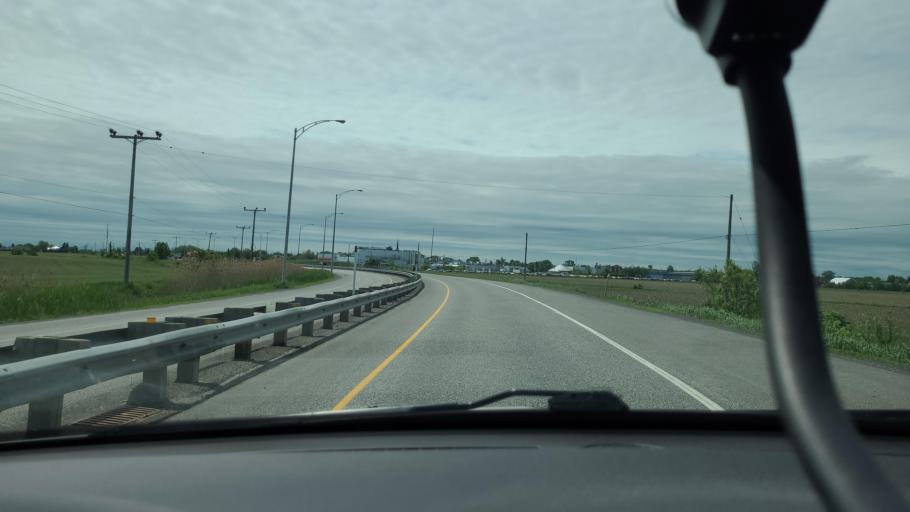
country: CA
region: Quebec
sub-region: Lanaudiere
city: Sainte-Julienne
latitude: 45.9113
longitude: -73.6567
